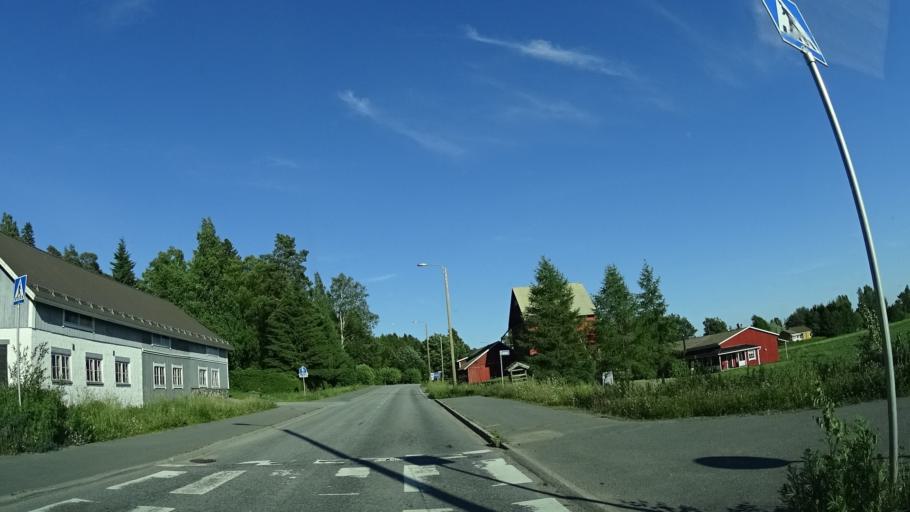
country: FI
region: Satakunta
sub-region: Pori
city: Ulvila
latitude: 61.5032
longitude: 21.8818
